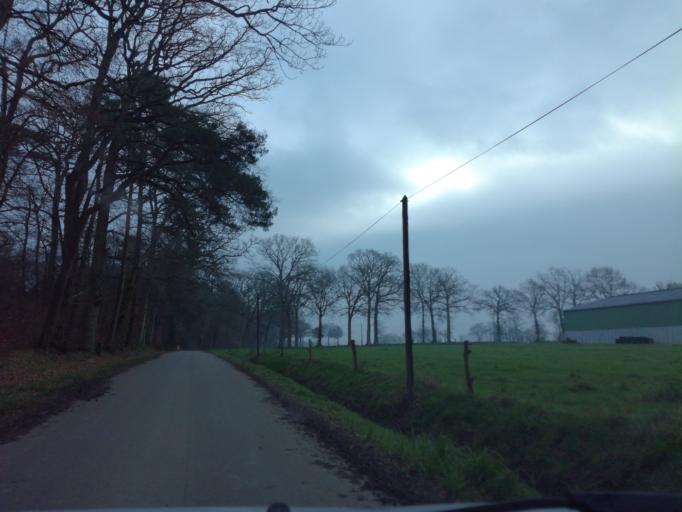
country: FR
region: Brittany
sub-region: Departement d'Ille-et-Vilaine
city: Gosne
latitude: 48.2622
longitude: -1.4700
